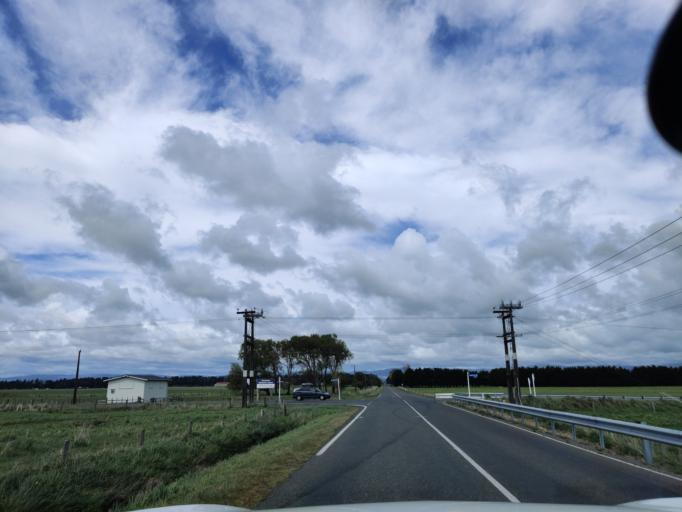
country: NZ
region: Manawatu-Wanganui
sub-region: Palmerston North City
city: Palmerston North
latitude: -40.3340
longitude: 175.5154
